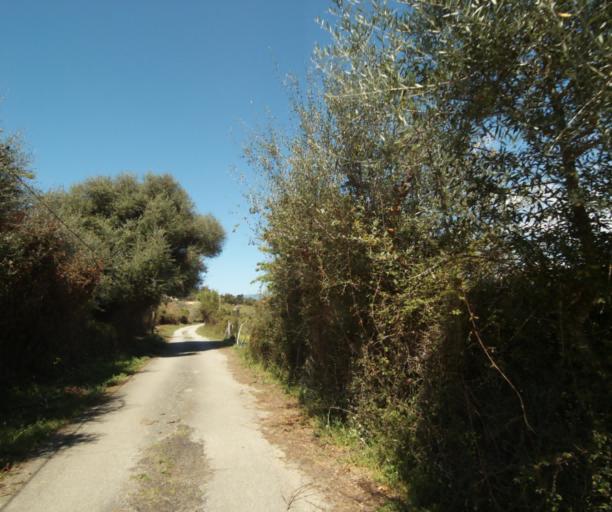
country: FR
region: Corsica
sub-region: Departement de la Corse-du-Sud
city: Propriano
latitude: 41.6422
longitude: 8.8704
